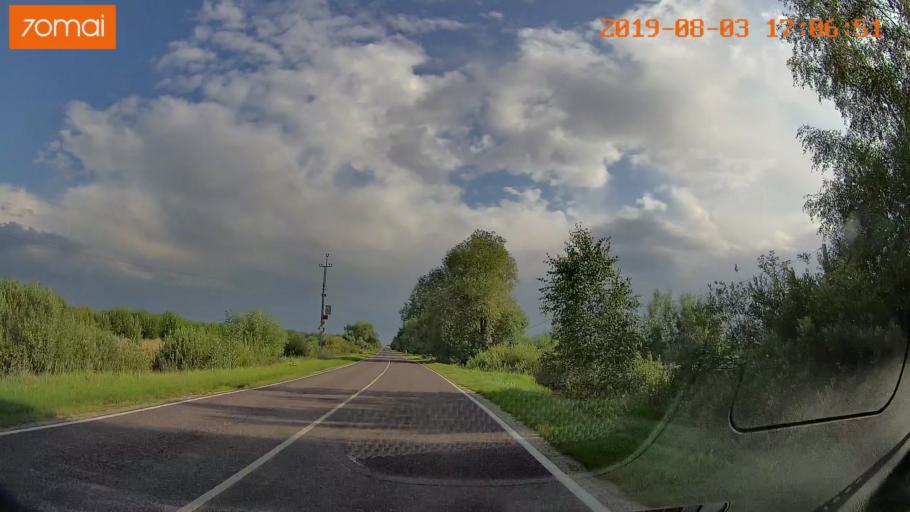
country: RU
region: Moskovskaya
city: Troitskoye
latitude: 55.3035
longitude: 38.5484
